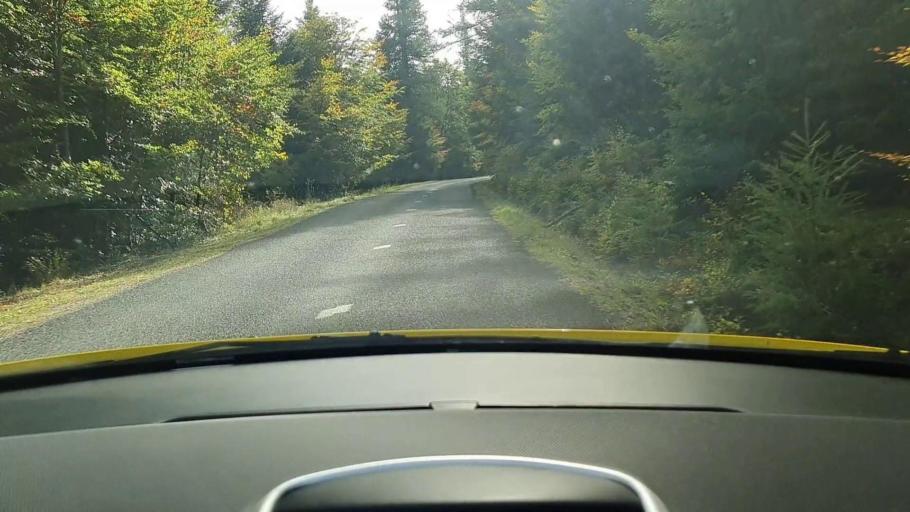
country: FR
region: Languedoc-Roussillon
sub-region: Departement du Gard
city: Valleraugue
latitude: 44.0757
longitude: 3.5658
